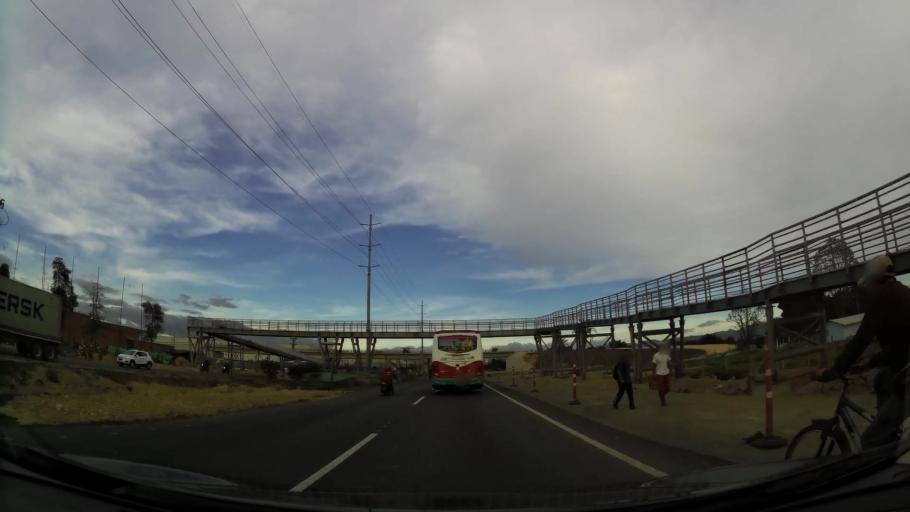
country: CO
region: Cundinamarca
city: Funza
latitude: 4.6980
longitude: -74.2028
